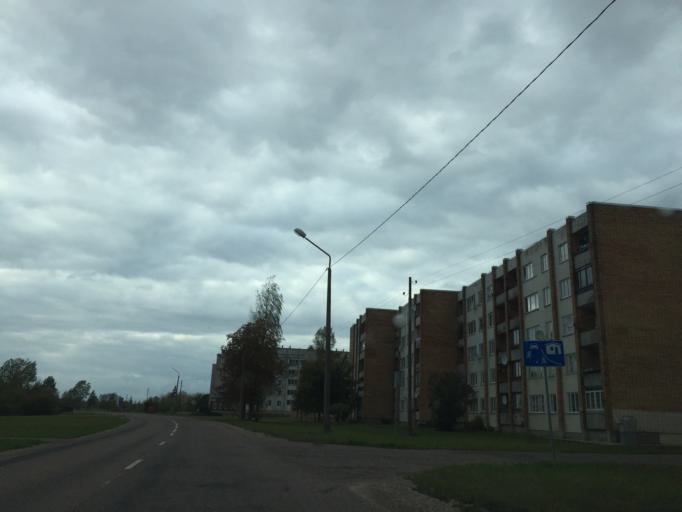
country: LV
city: Tireli
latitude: 56.7992
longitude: 23.6107
